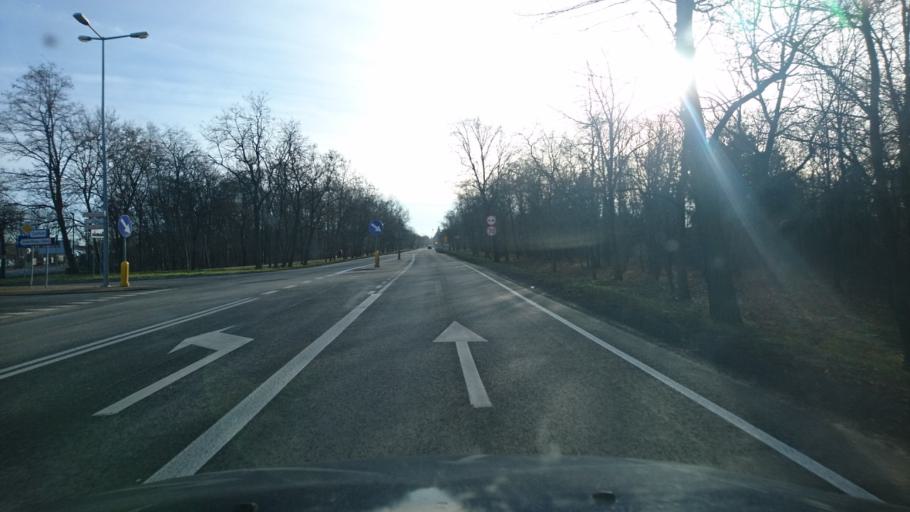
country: PL
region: Greater Poland Voivodeship
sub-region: Powiat ostrzeszowski
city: Ostrzeszow
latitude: 51.4342
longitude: 17.9163
